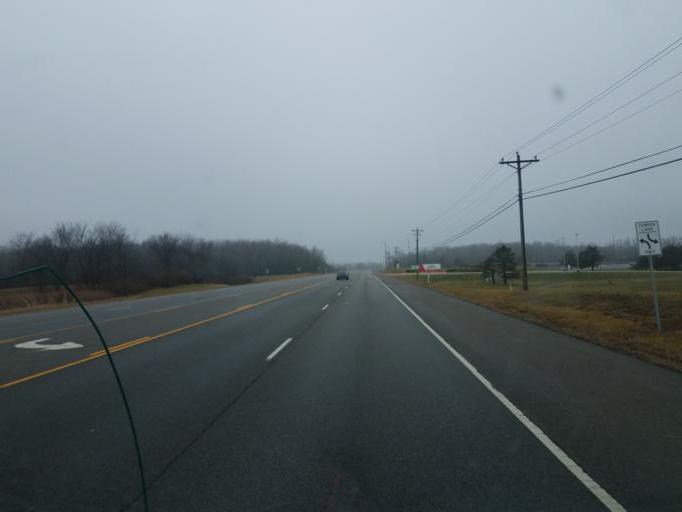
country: US
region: Ohio
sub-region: Champaign County
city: North Lewisburg
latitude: 40.2771
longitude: -83.5227
